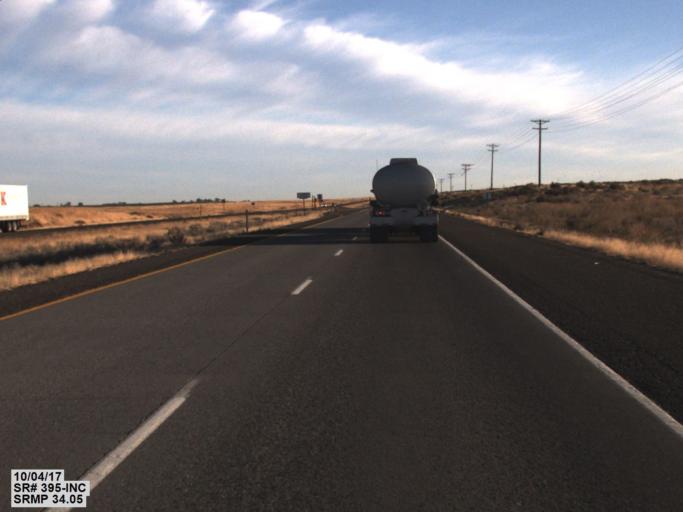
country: US
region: Washington
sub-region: Franklin County
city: Pasco
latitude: 46.4081
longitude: -119.0507
